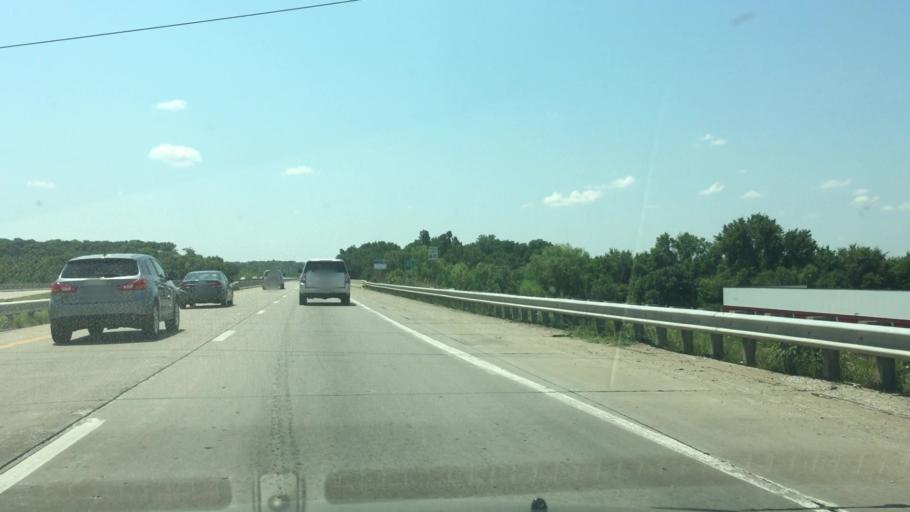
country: US
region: Missouri
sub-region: Jackson County
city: Grandview
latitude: 38.8724
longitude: -94.6028
